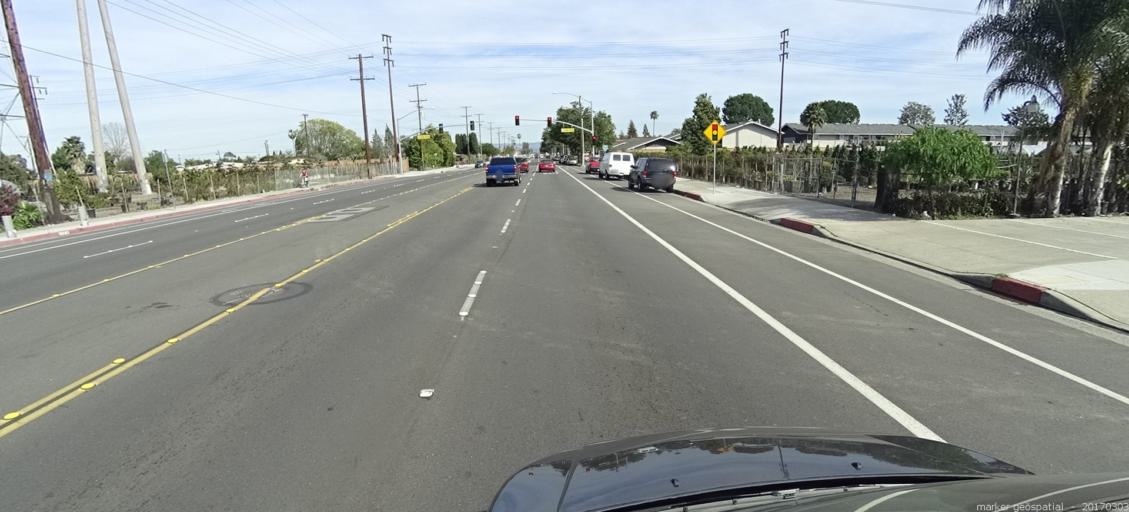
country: US
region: California
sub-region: Orange County
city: Stanton
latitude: 33.8175
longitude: -117.9813
